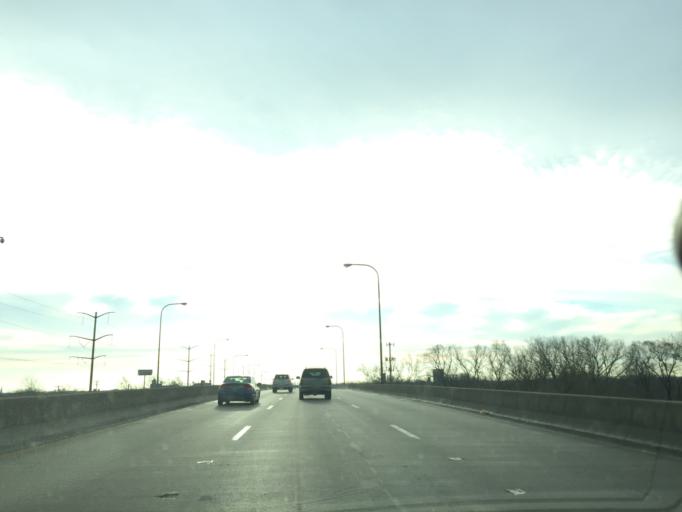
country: US
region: Illinois
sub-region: Cook County
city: Chicago
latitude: 41.7570
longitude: -87.5959
